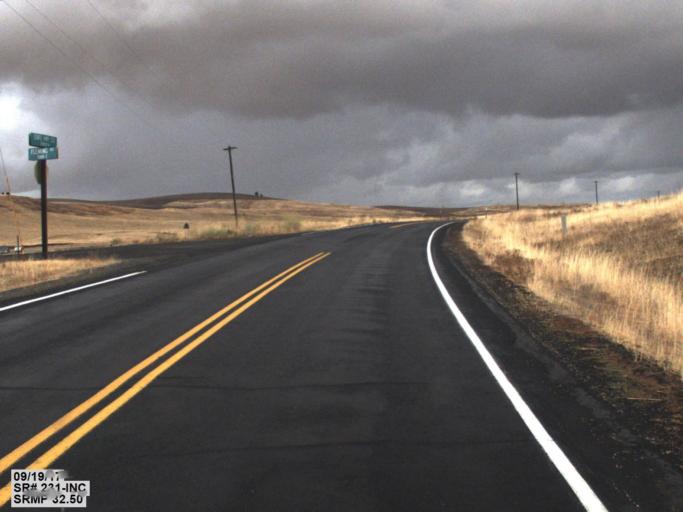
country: US
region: Washington
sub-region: Spokane County
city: Medical Lake
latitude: 47.6897
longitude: -117.8824
